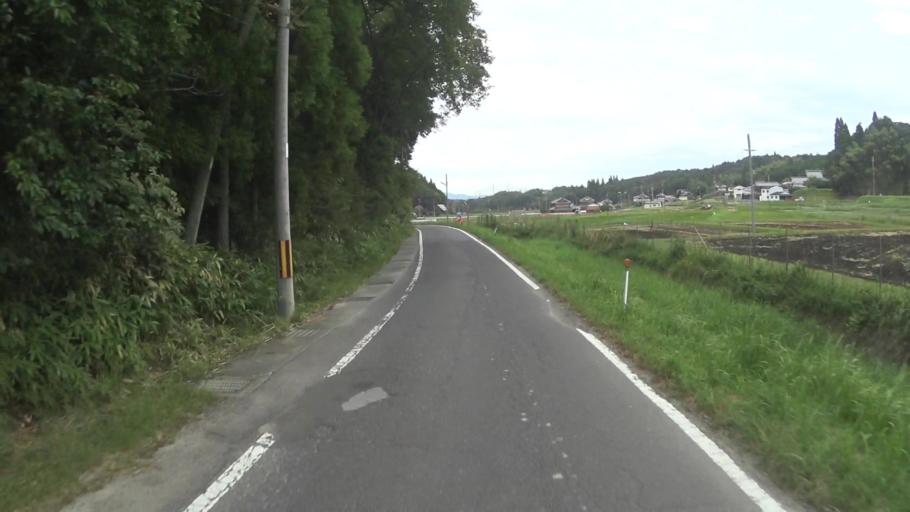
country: JP
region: Mie
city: Ueno-ebisumachi
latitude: 34.8475
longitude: 136.0127
